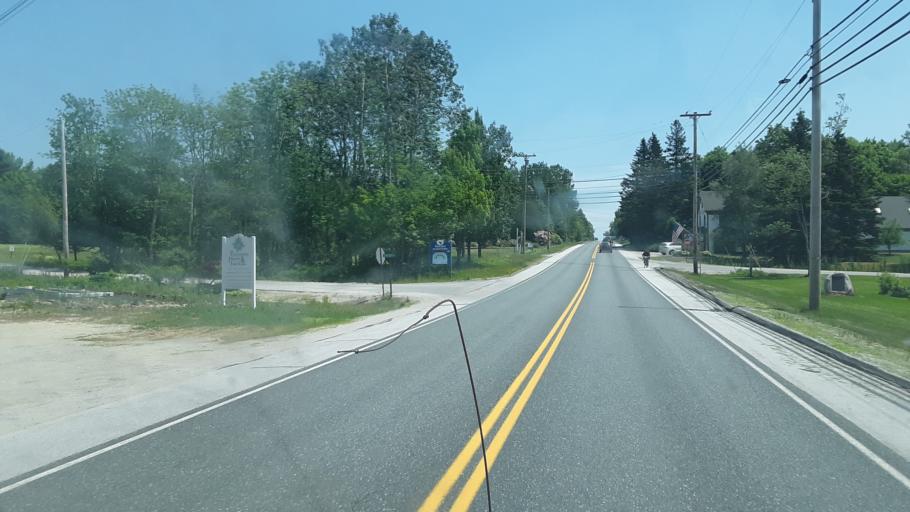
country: US
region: Maine
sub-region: Hancock County
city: Hancock
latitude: 44.5287
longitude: -68.2538
